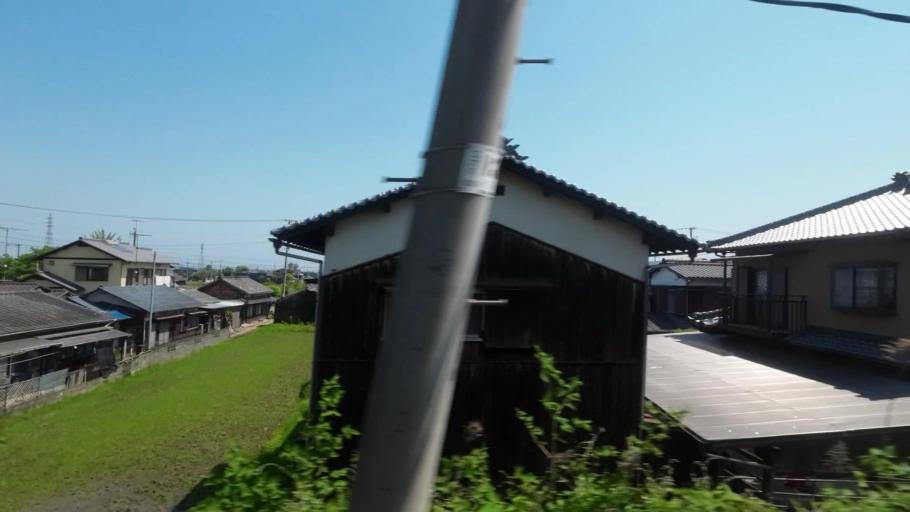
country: JP
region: Ehime
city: Saijo
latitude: 33.9373
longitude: 133.0789
